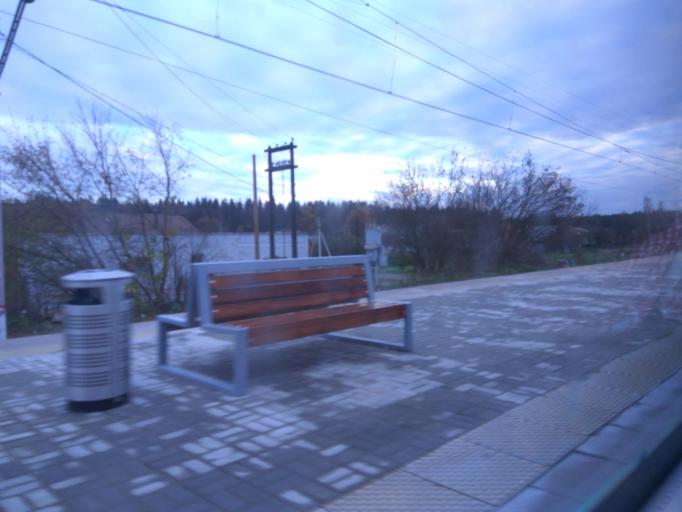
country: RU
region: Moskovskaya
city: Kievskij
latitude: 55.4795
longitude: 36.9157
